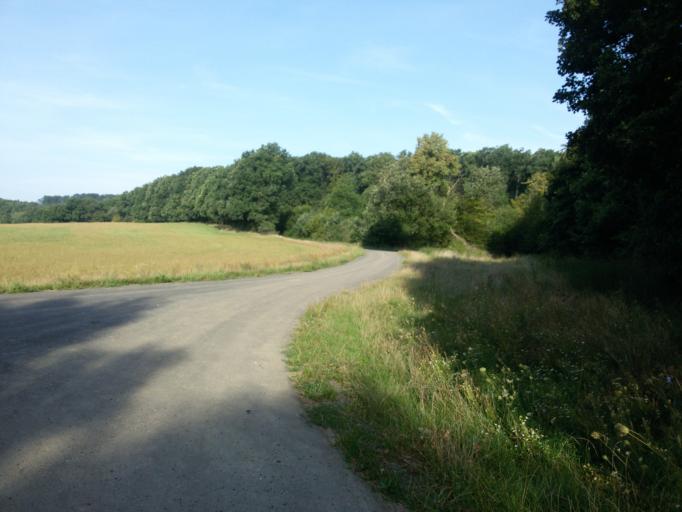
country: CZ
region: Zlin
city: Brezolupy
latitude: 49.0744
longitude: 17.6002
